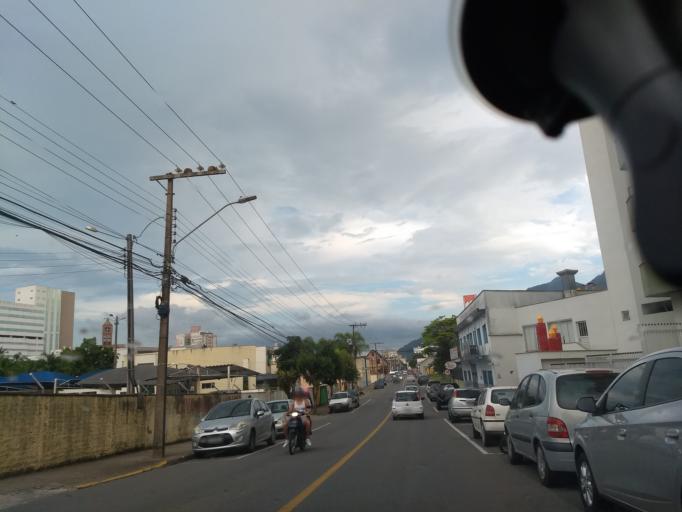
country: BR
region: Santa Catarina
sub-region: Jaragua Do Sul
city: Jaragua do Sul
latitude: -26.4799
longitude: -49.0879
